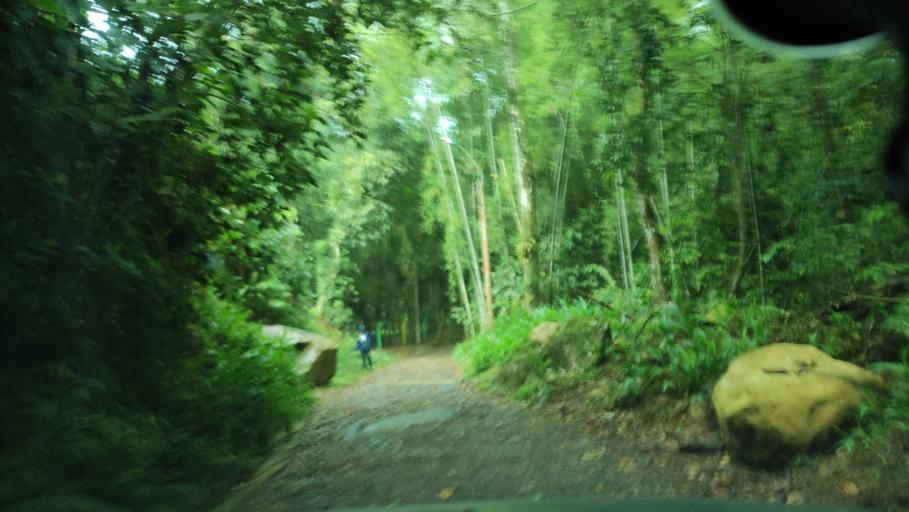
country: CO
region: Valle del Cauca
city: Jamundi
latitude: 3.3241
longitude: -76.6319
